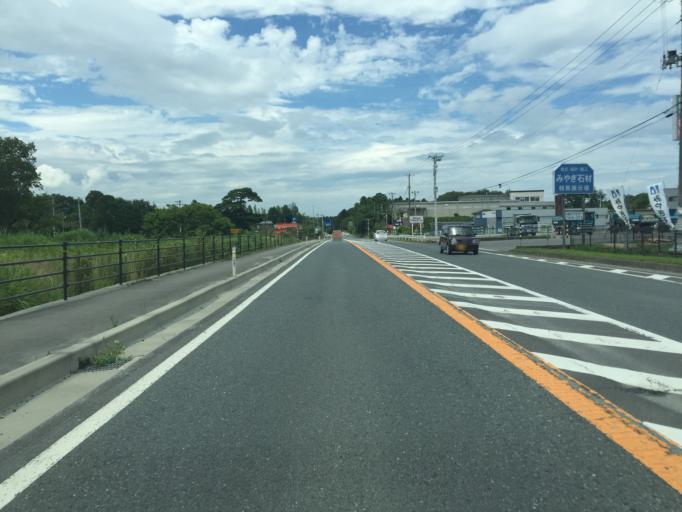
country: JP
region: Miyagi
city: Marumori
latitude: 37.7467
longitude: 140.9544
